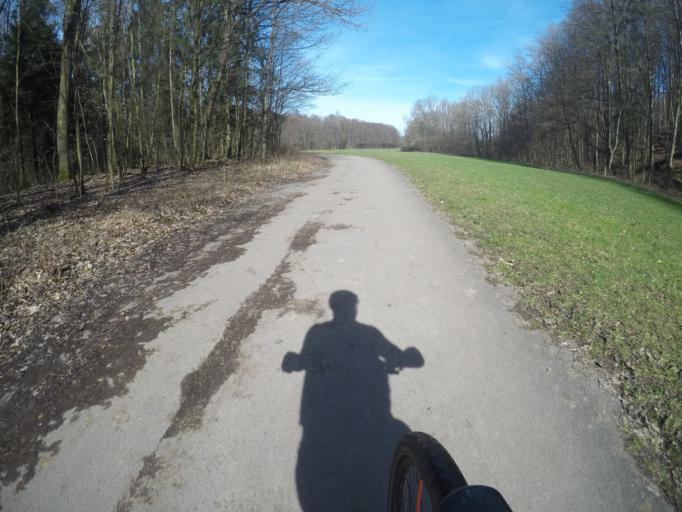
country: DE
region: Baden-Wuerttemberg
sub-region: Regierungsbezirk Stuttgart
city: Korntal
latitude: 48.7989
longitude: 9.1134
